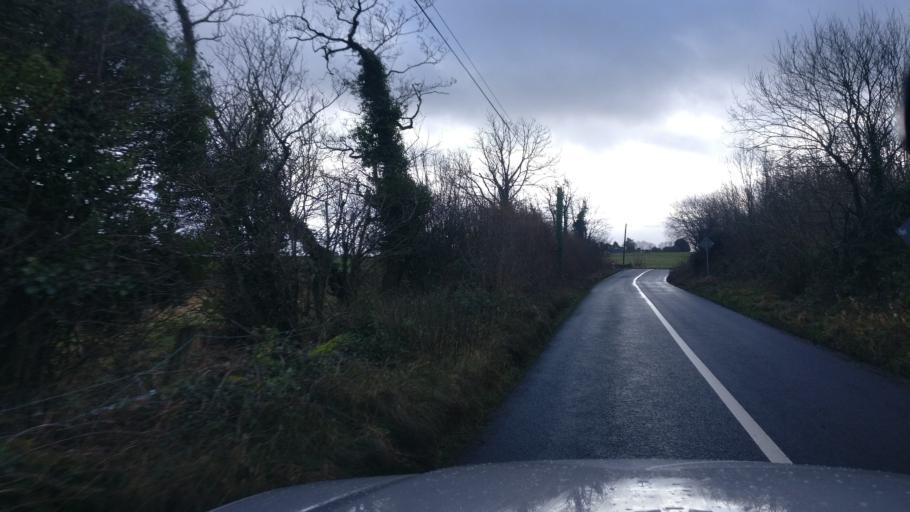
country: IE
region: Connaught
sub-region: County Galway
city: Loughrea
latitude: 53.2410
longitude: -8.6209
